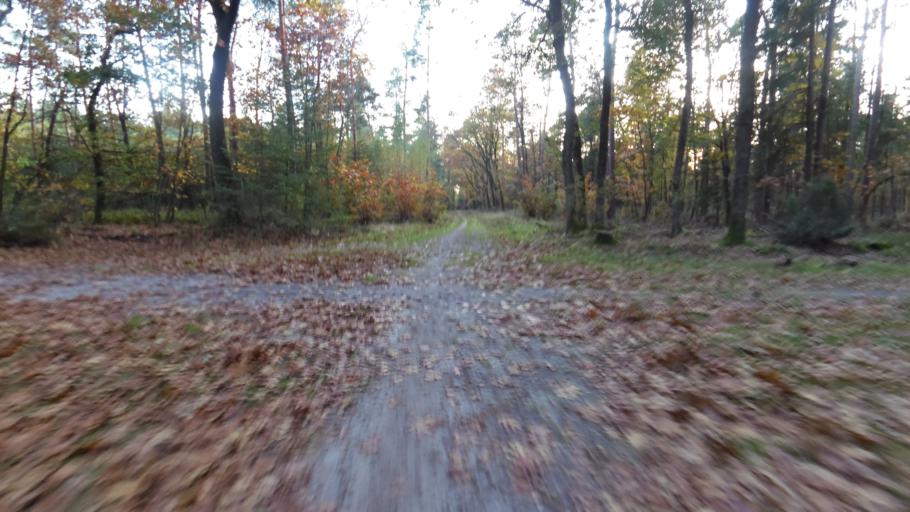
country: NL
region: Gelderland
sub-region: Gemeente Epe
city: Epe
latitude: 52.3666
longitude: 5.9692
